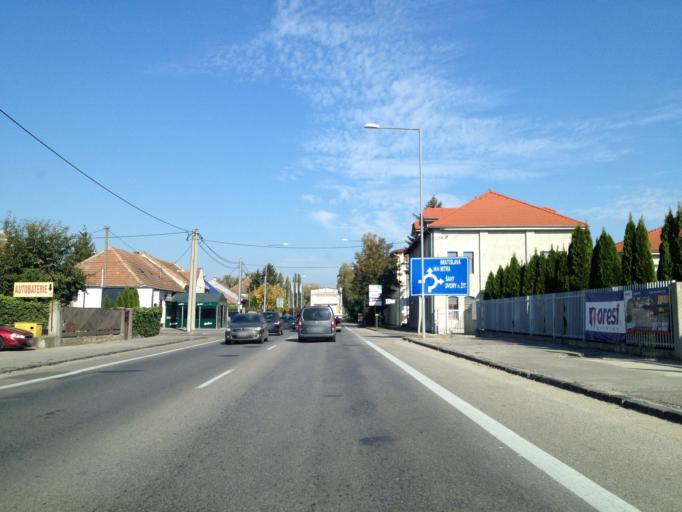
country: SK
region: Nitriansky
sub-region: Okres Nove Zamky
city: Nove Zamky
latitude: 47.9815
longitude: 18.1767
